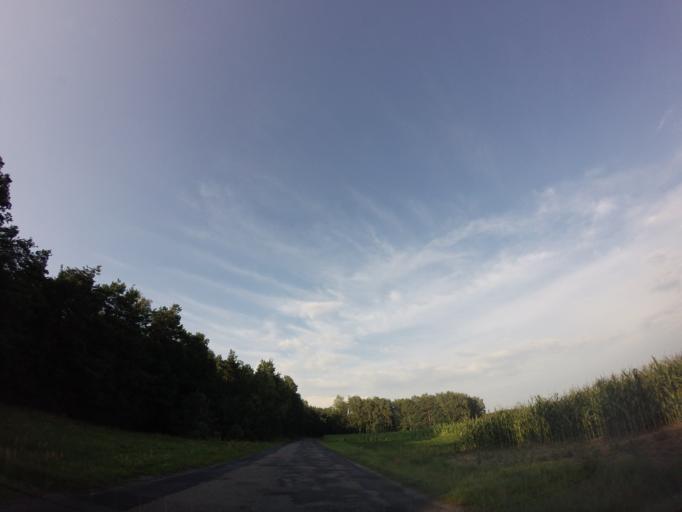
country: PL
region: Lublin Voivodeship
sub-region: Powiat pulawski
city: Kurow
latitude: 51.4285
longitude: 22.2109
